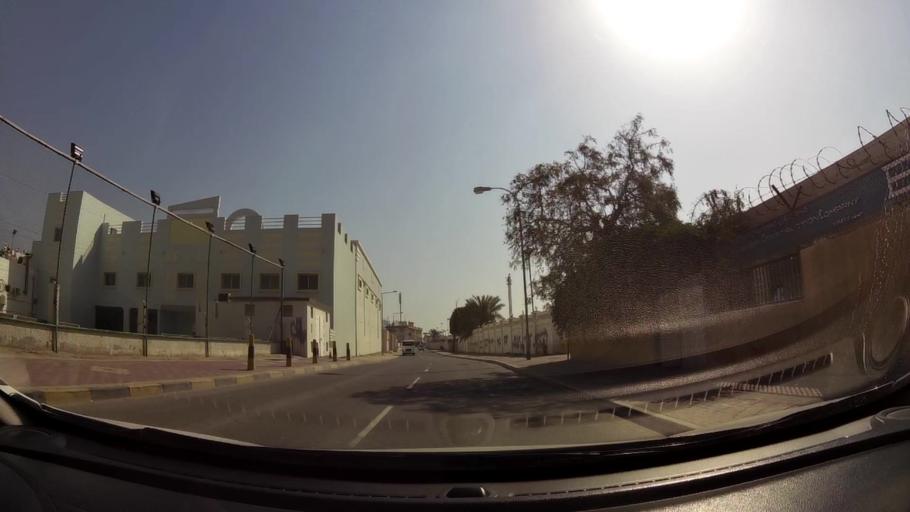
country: BH
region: Manama
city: Manama
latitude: 26.2095
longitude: 50.6011
